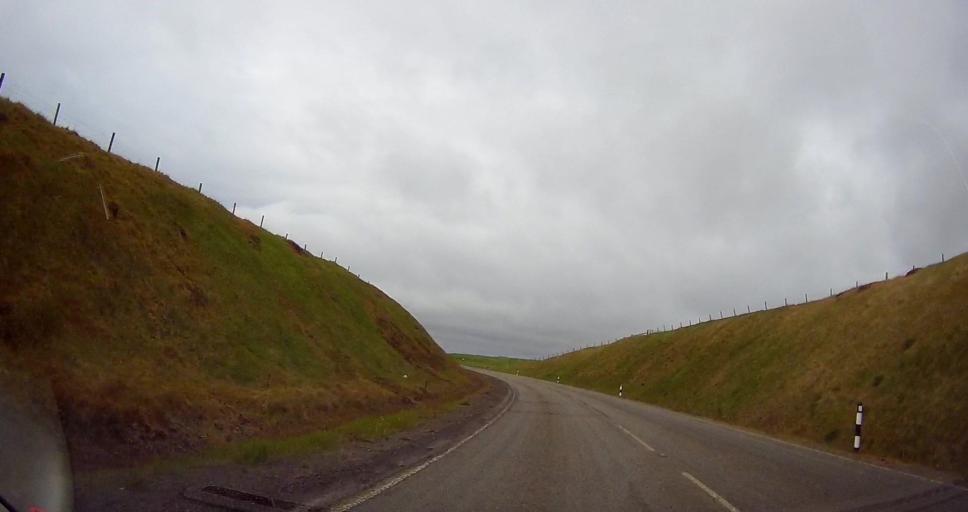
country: GB
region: Scotland
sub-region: Shetland Islands
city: Lerwick
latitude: 60.3714
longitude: -1.3177
